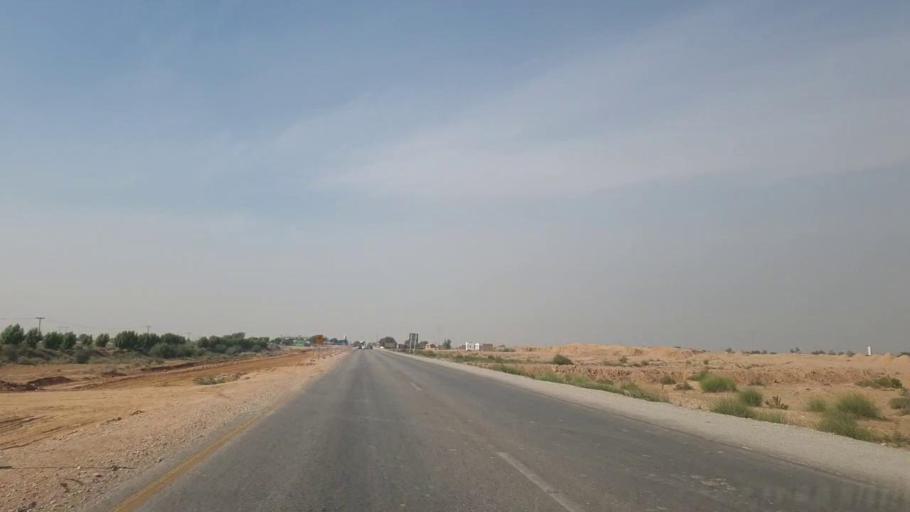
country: PK
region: Sindh
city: Sann
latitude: 26.0247
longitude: 68.1297
